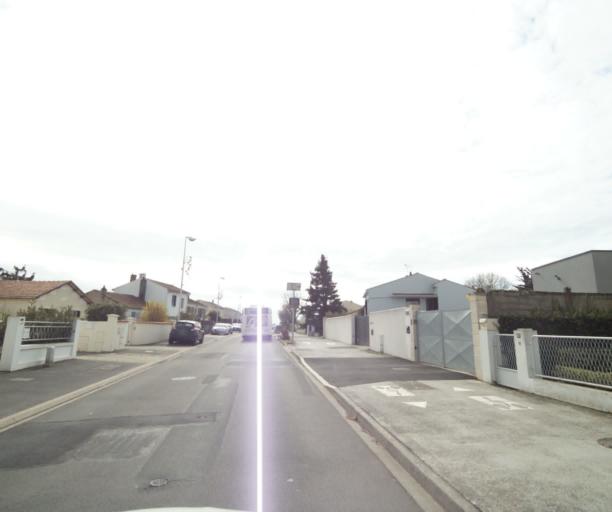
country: FR
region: Poitou-Charentes
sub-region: Departement de la Charente-Maritime
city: Lagord
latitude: 46.1849
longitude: -1.1588
